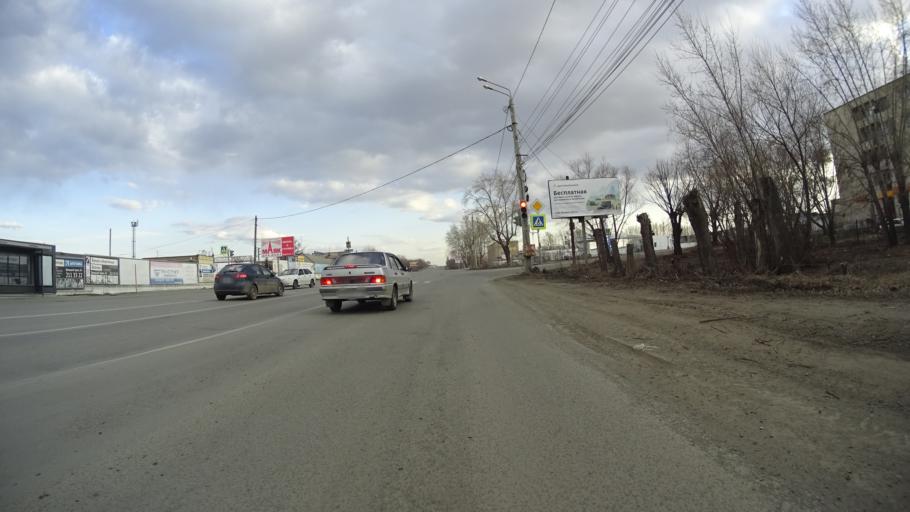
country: RU
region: Chelyabinsk
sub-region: Gorod Chelyabinsk
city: Chelyabinsk
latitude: 55.1075
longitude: 61.3870
